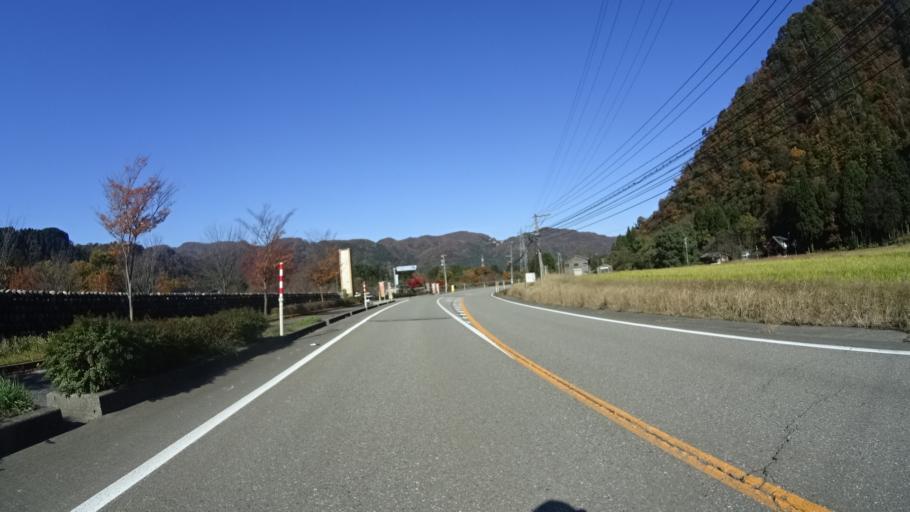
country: JP
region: Ishikawa
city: Tsurugi-asahimachi
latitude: 36.3647
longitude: 136.6130
